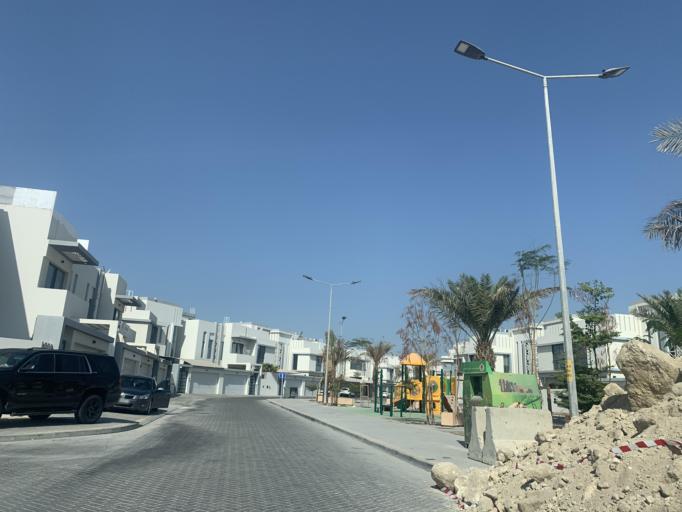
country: BH
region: Central Governorate
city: Madinat Hamad
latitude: 26.1324
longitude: 50.4830
